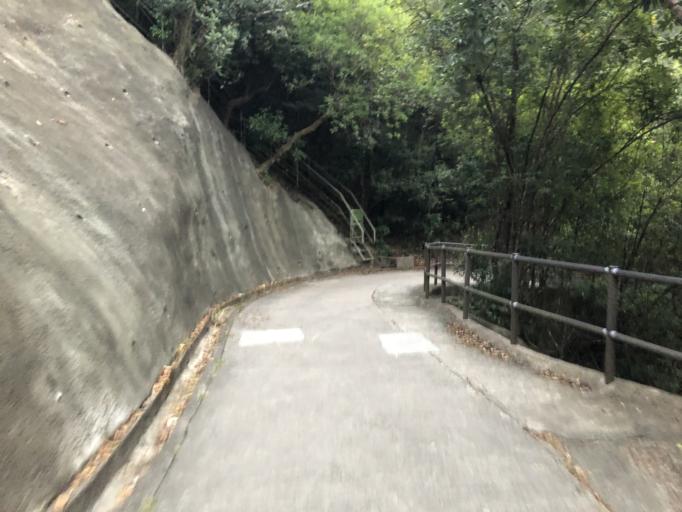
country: HK
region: Wanchai
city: Wan Chai
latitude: 22.2599
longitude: 114.2118
